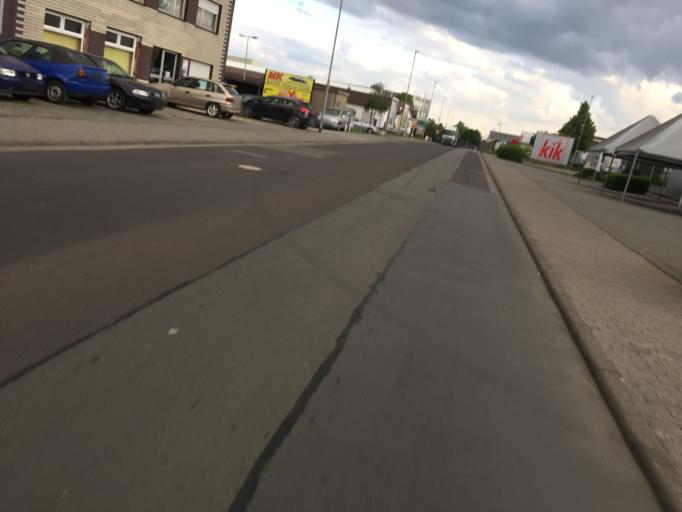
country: DE
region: Hesse
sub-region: Regierungsbezirk Darmstadt
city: Butzbach
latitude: 50.4349
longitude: 8.6820
